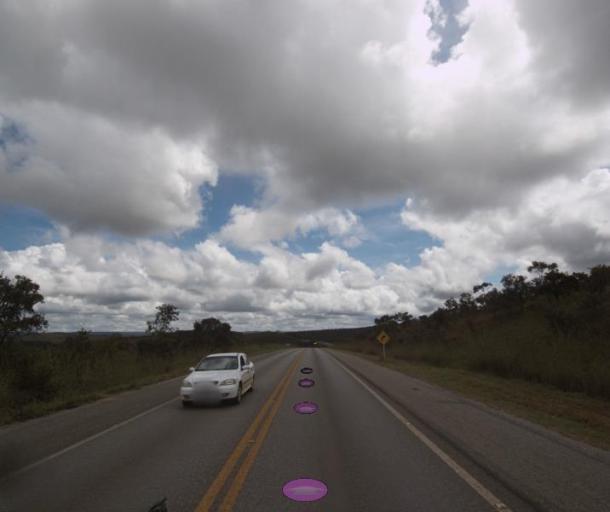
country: BR
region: Goias
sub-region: Pirenopolis
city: Pirenopolis
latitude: -15.7520
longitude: -48.5926
